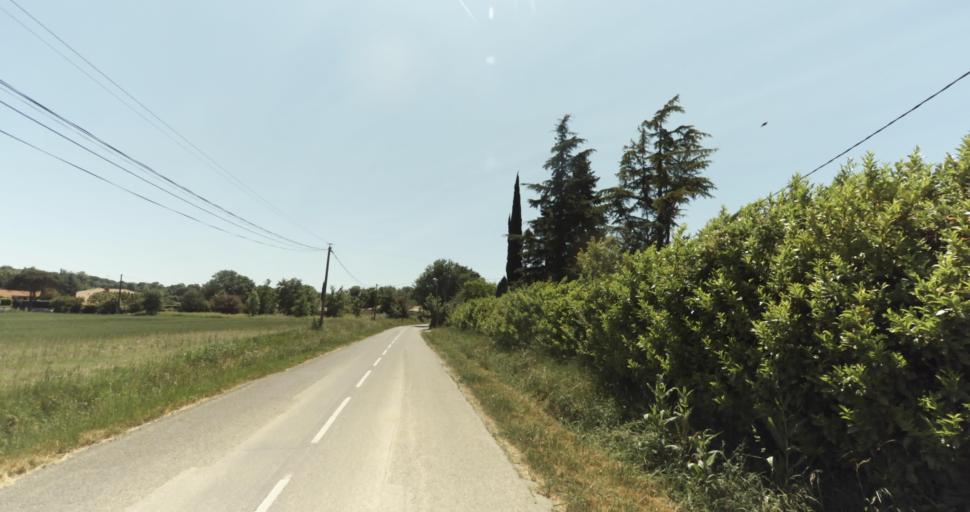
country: FR
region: Midi-Pyrenees
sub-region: Departement de la Haute-Garonne
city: Levignac
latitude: 43.6425
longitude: 1.1743
